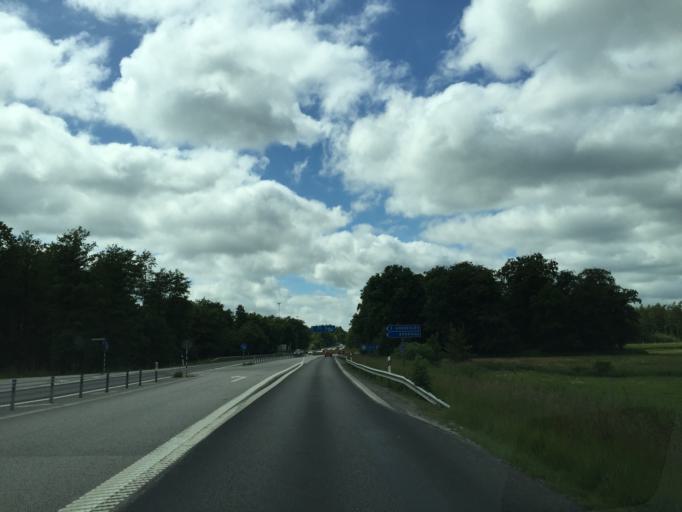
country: SE
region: Skane
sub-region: Trelleborgs Kommun
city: Anderslov
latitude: 55.5080
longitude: 13.3294
